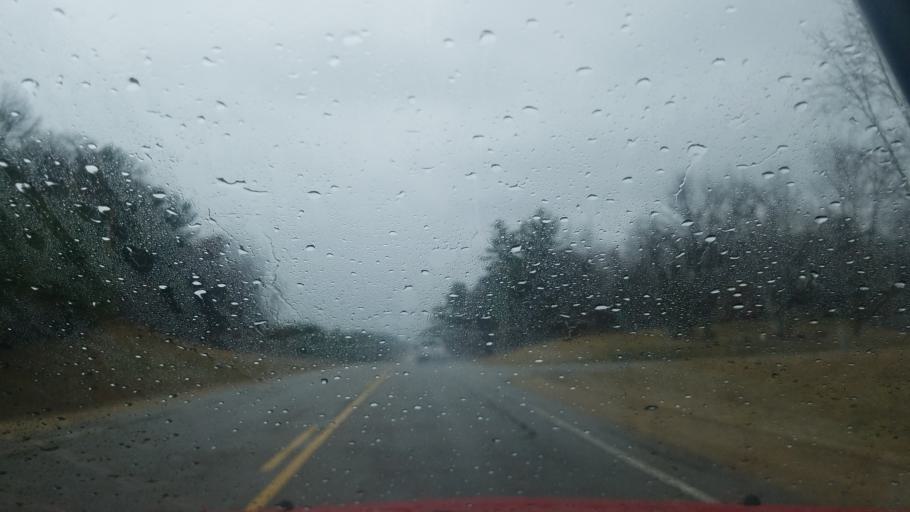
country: US
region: Wisconsin
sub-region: Dunn County
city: Tainter Lake
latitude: 44.9745
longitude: -91.8943
